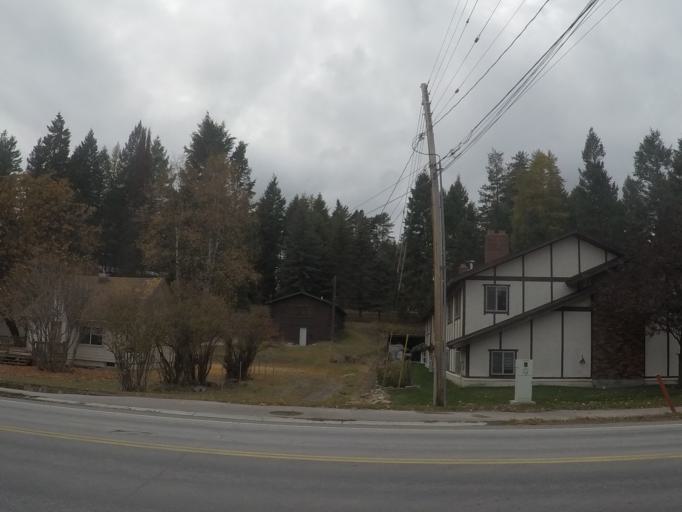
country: US
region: Montana
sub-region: Flathead County
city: Whitefish
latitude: 48.4216
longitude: -114.3410
